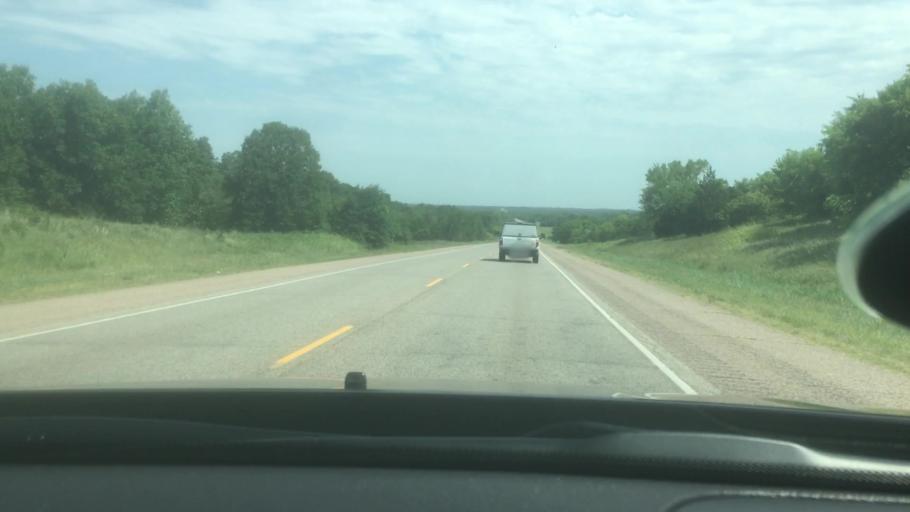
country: US
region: Oklahoma
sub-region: Seminole County
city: Maud
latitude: 35.0609
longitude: -96.9314
